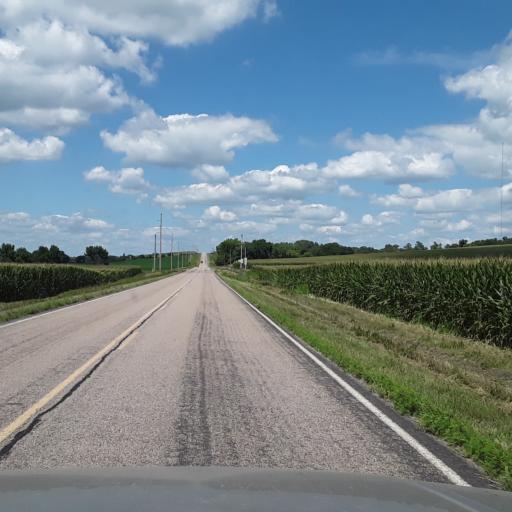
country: US
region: Nebraska
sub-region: Nance County
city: Genoa
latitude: 41.5100
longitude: -97.6959
